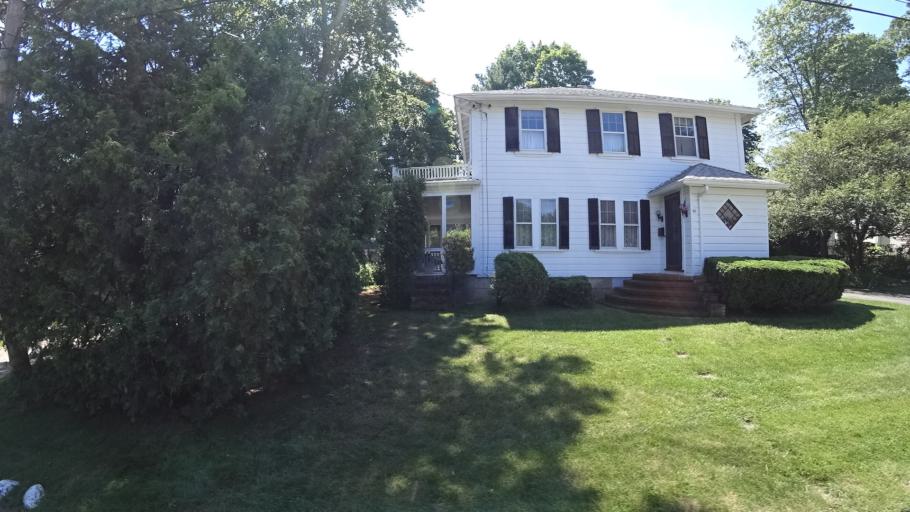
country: US
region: Massachusetts
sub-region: Norfolk County
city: Dedham
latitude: 42.2441
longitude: -71.1576
